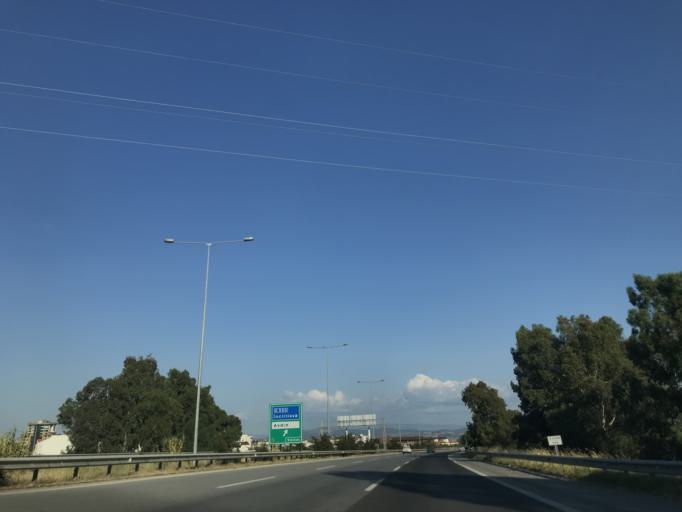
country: TR
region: Aydin
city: Aydin
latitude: 37.8567
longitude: 27.8009
